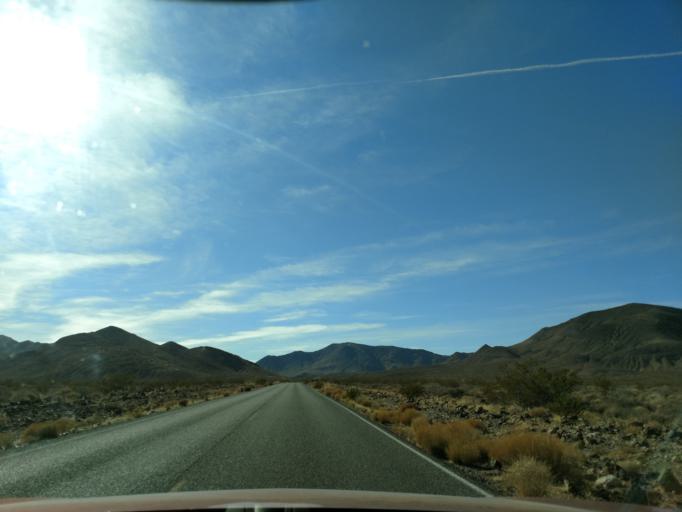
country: US
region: Nevada
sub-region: Nye County
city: Beatty
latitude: 36.8155
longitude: -116.9017
